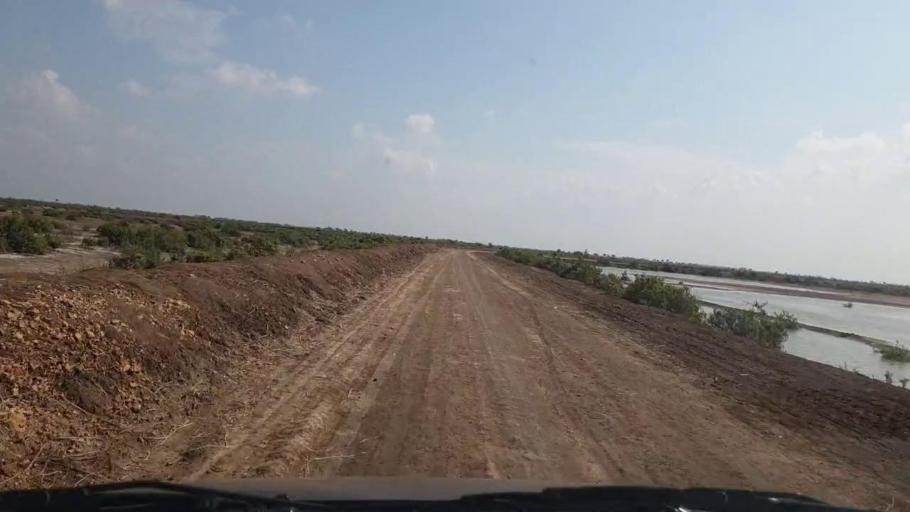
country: PK
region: Sindh
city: Badin
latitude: 24.4973
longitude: 68.6103
